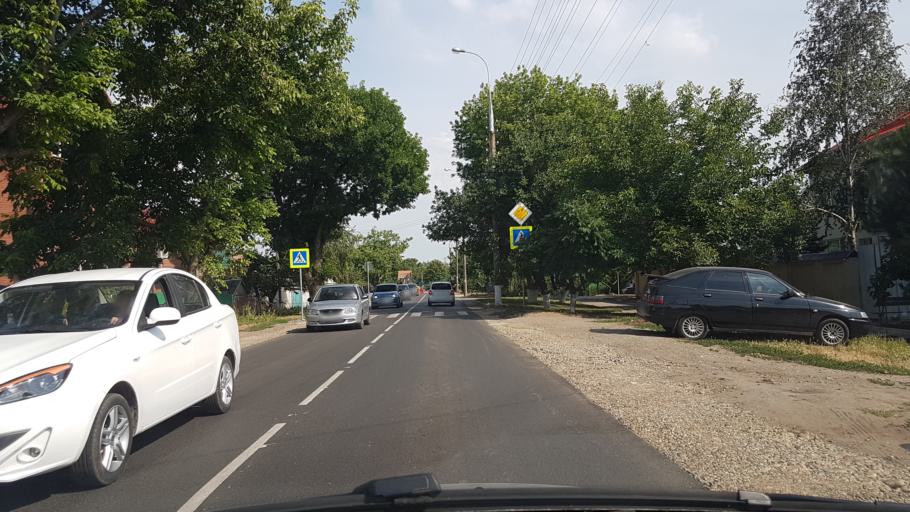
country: RU
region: Krasnodarskiy
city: Pashkovskiy
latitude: 45.0277
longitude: 39.1252
